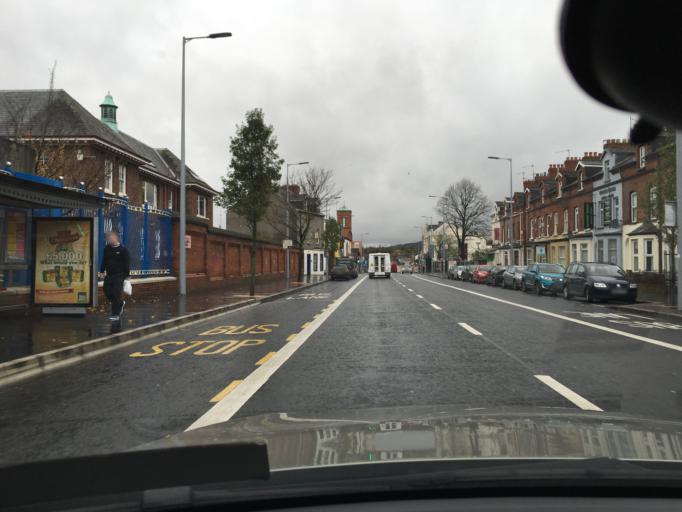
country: GB
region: Northern Ireland
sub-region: City of Belfast
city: Belfast
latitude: 54.5934
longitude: -5.9584
